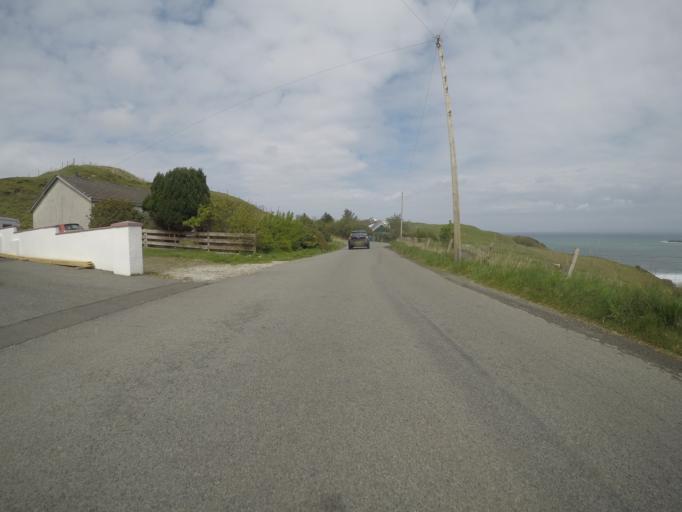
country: GB
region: Scotland
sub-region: Highland
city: Portree
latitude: 57.6382
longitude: -6.2417
